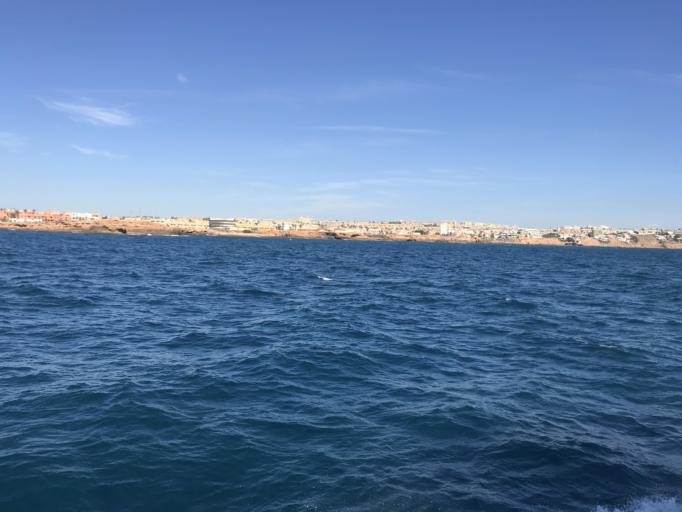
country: ES
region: Valencia
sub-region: Provincia de Alicante
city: Torrevieja
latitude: 37.9833
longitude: -0.6513
